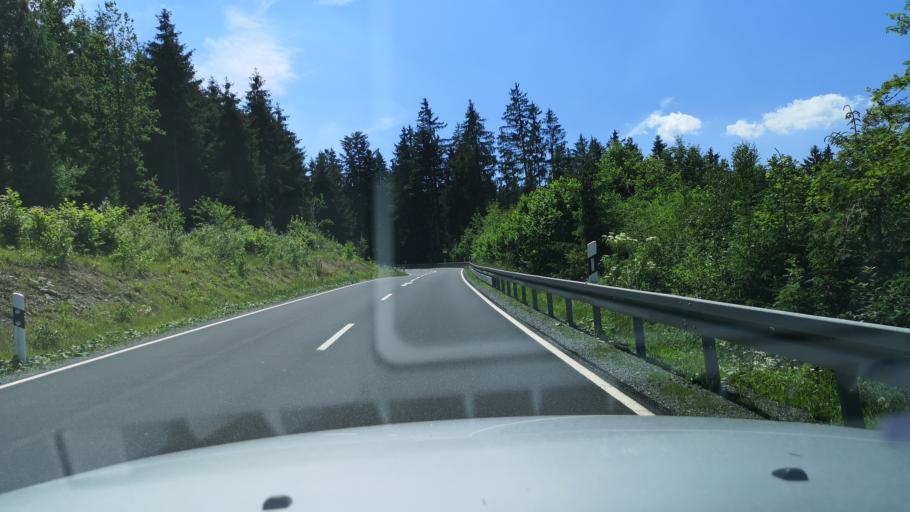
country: DE
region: Bavaria
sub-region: Upper Franconia
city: Teuschnitz
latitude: 50.3861
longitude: 11.3625
